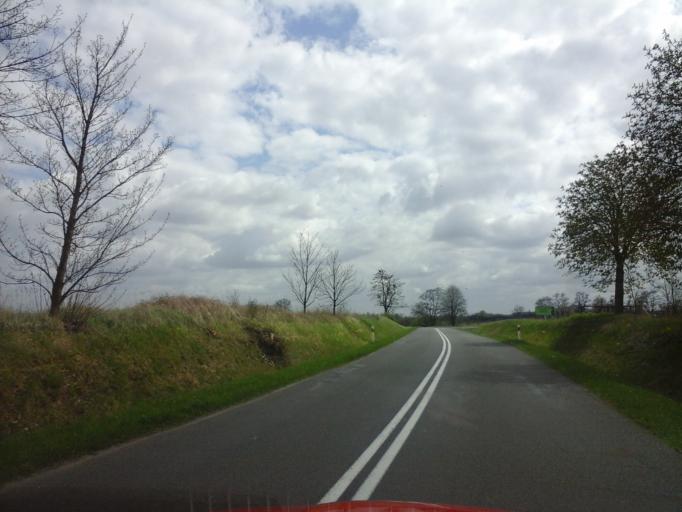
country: PL
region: West Pomeranian Voivodeship
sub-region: Powiat choszczenski
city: Bierzwnik
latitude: 53.0546
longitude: 15.6624
